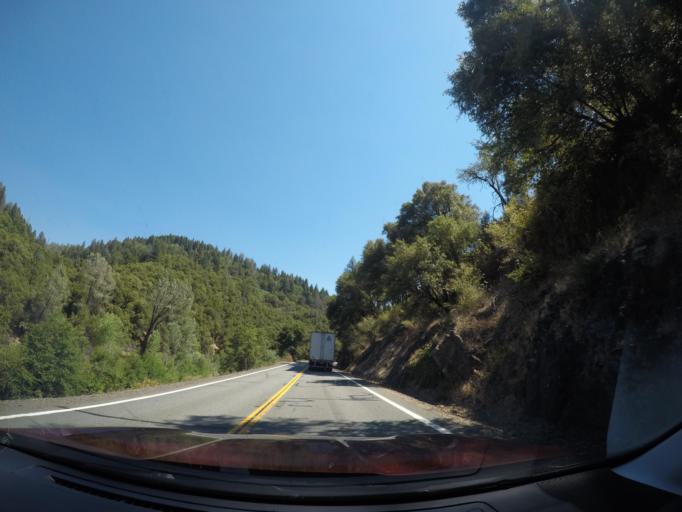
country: US
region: California
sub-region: Shasta County
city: Bella Vista
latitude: 40.7302
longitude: -122.0764
